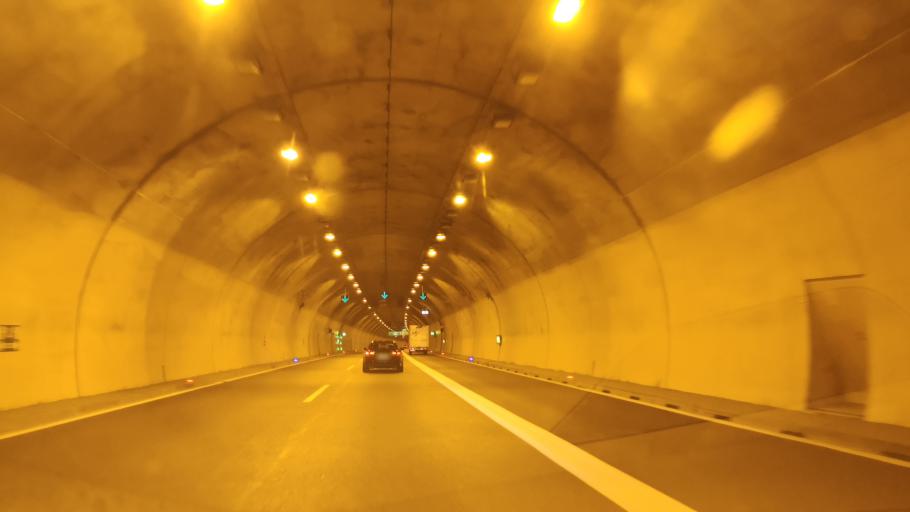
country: SI
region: Ljubljana
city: Ljubljana
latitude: 46.0895
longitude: 14.4607
